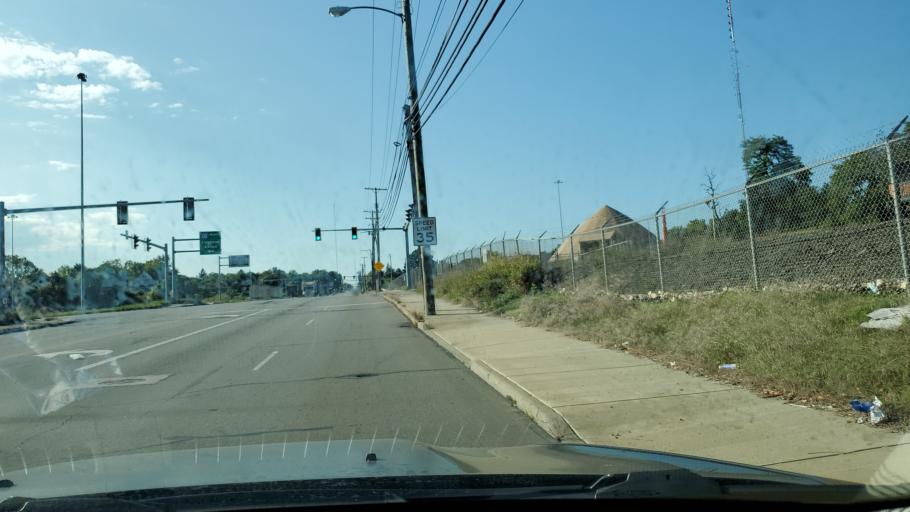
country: US
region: Ohio
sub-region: Mahoning County
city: Youngstown
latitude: 41.0834
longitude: -80.6464
